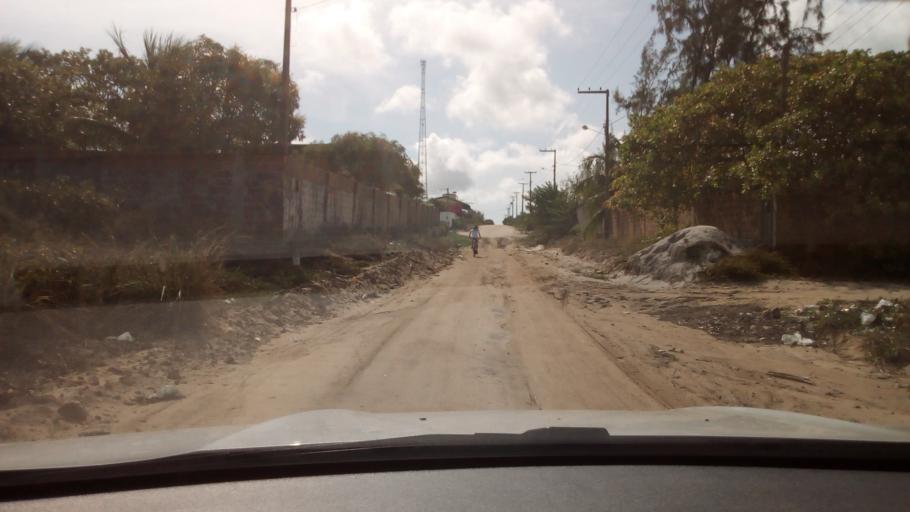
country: BR
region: Paraiba
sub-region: Conde
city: Conde
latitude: -7.3057
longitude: -34.8070
